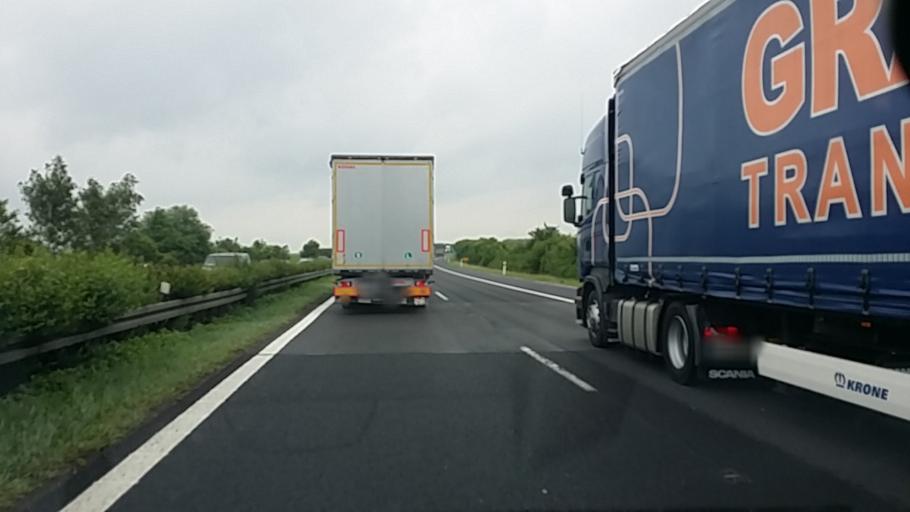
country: CZ
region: Ustecky
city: Lovosice
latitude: 50.5026
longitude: 14.0570
